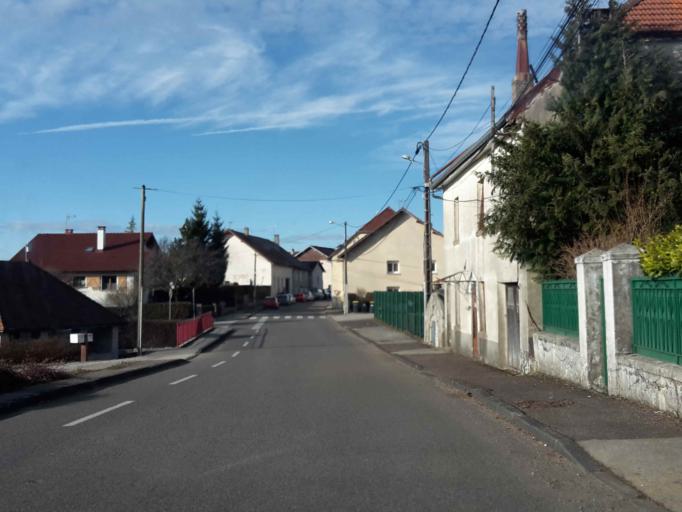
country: FR
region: Franche-Comte
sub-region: Departement du Doubs
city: Vercel-Villedieu-le-Camp
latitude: 47.1806
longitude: 6.3987
